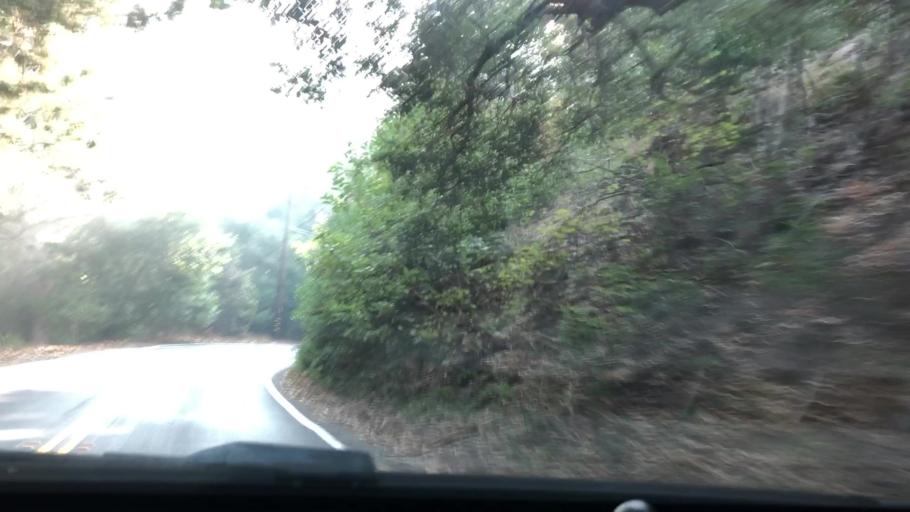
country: US
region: California
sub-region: Alameda County
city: Berkeley
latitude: 37.8865
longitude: -122.2433
